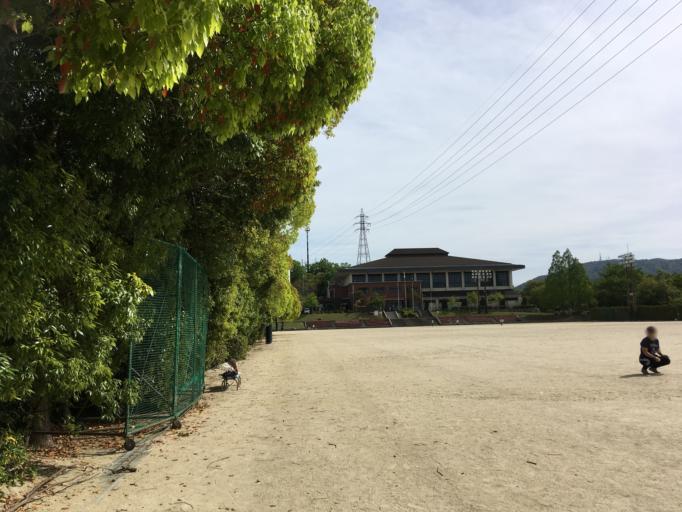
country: JP
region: Nara
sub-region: Ikoma-shi
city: Ikoma
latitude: 34.7134
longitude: 135.7114
